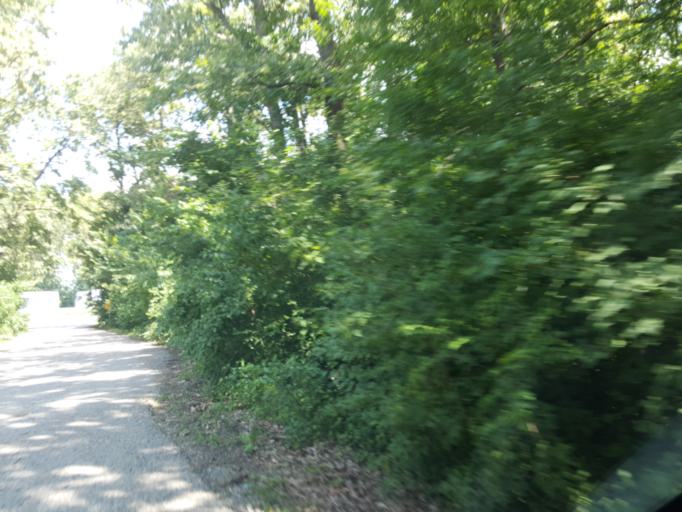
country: RS
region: Autonomna Pokrajina Vojvodina
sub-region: Sremski Okrug
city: Sid
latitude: 45.0427
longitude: 19.1383
